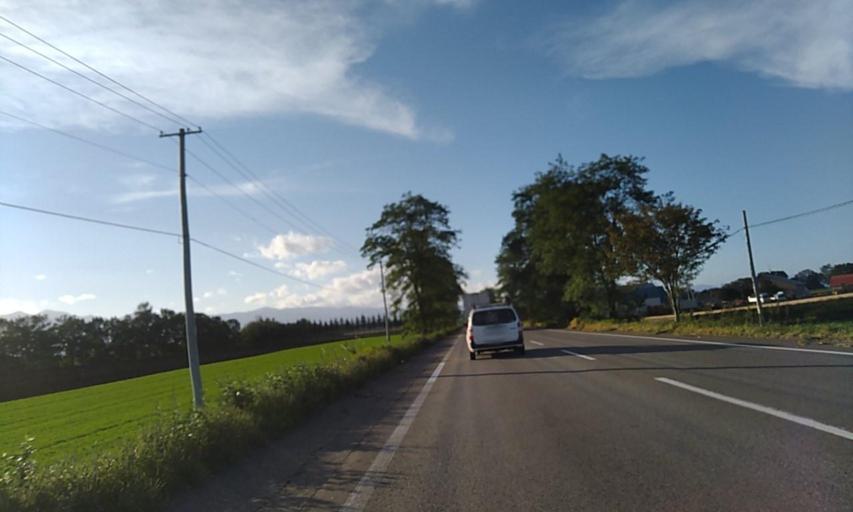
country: JP
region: Hokkaido
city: Obihiro
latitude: 42.9254
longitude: 142.9877
